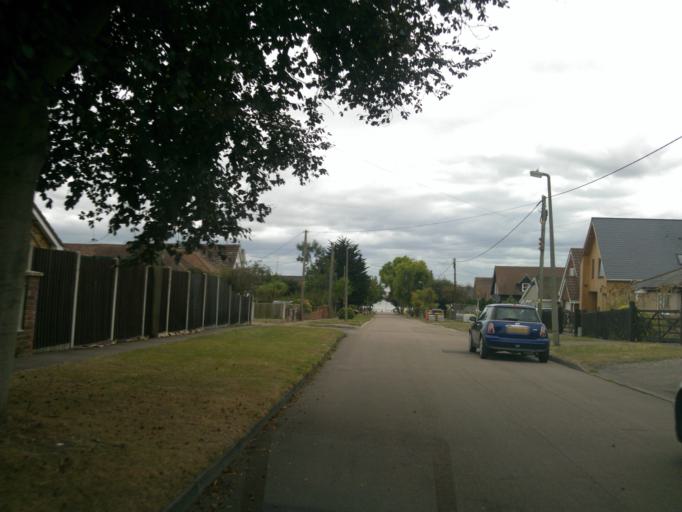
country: GB
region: England
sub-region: Essex
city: West Mersea
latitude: 51.7763
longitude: 0.9304
